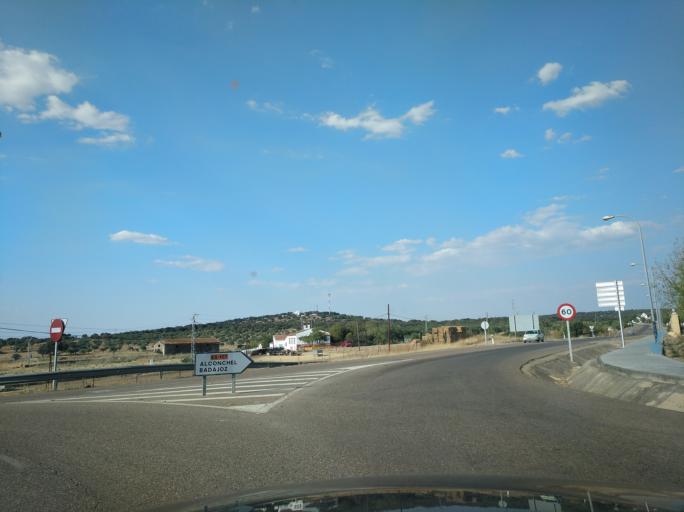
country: ES
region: Extremadura
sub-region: Provincia de Badajoz
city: Villanueva del Fresno
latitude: 38.3796
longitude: -7.1615
